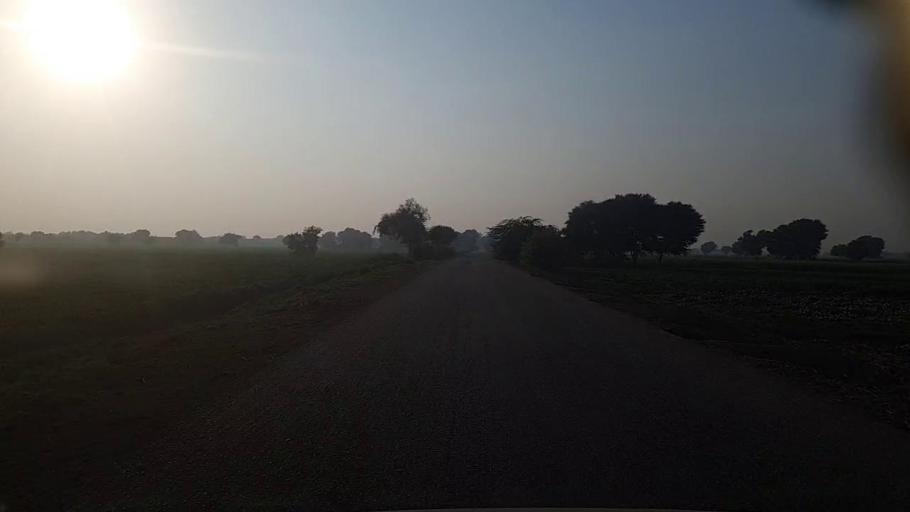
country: PK
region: Sindh
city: Pad Idan
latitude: 26.7183
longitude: 68.4117
